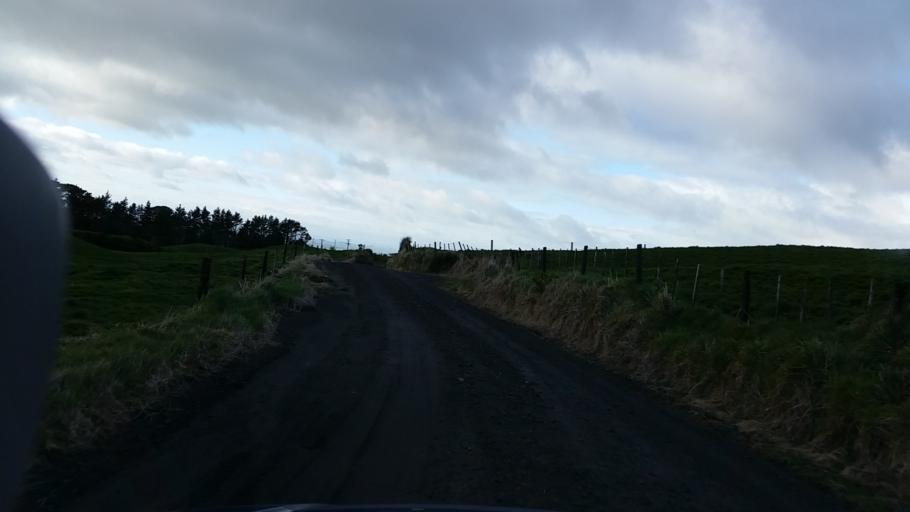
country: NZ
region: Taranaki
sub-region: South Taranaki District
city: Eltham
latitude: -39.3317
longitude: 174.1725
